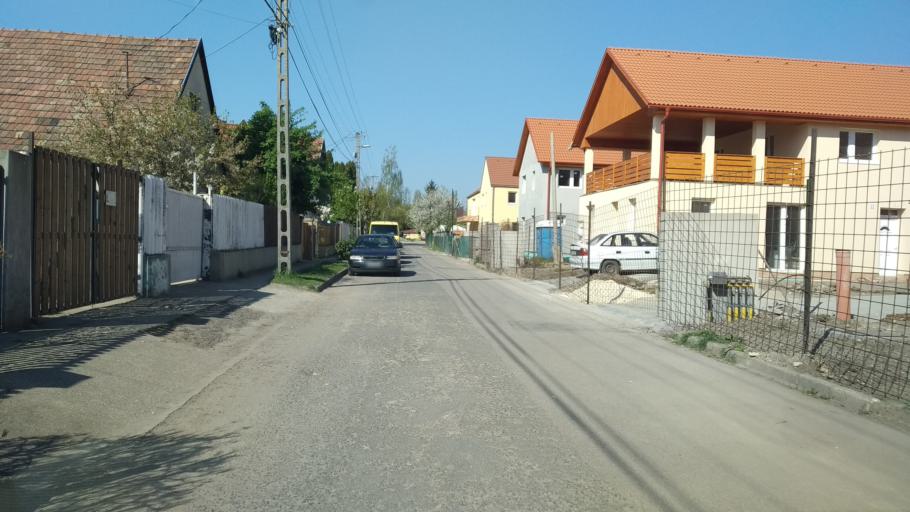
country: HU
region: Pest
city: Szentendre
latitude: 47.6606
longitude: 19.0705
